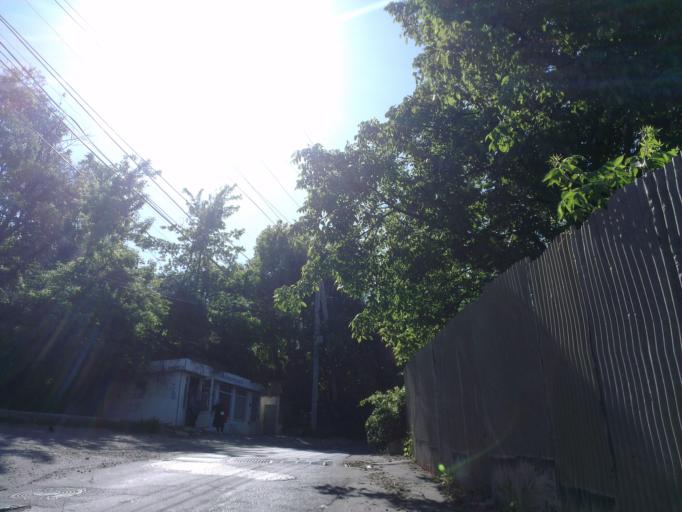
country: MD
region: Chisinau
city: Chisinau
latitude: 47.0167
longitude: 28.8223
